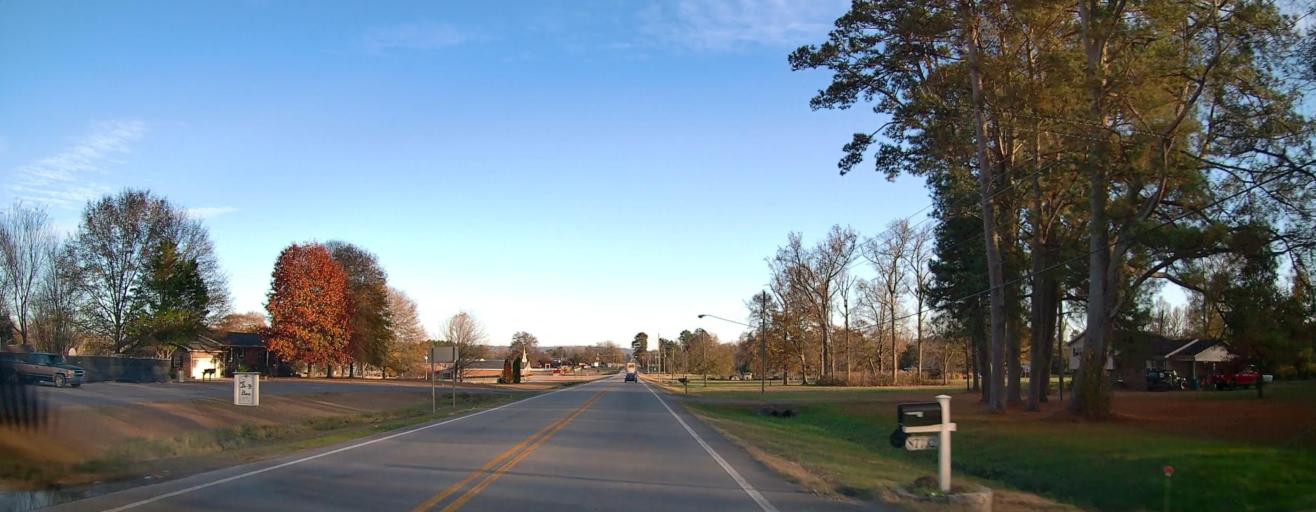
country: US
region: Alabama
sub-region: Blount County
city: Oneonta
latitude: 34.1140
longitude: -86.3864
